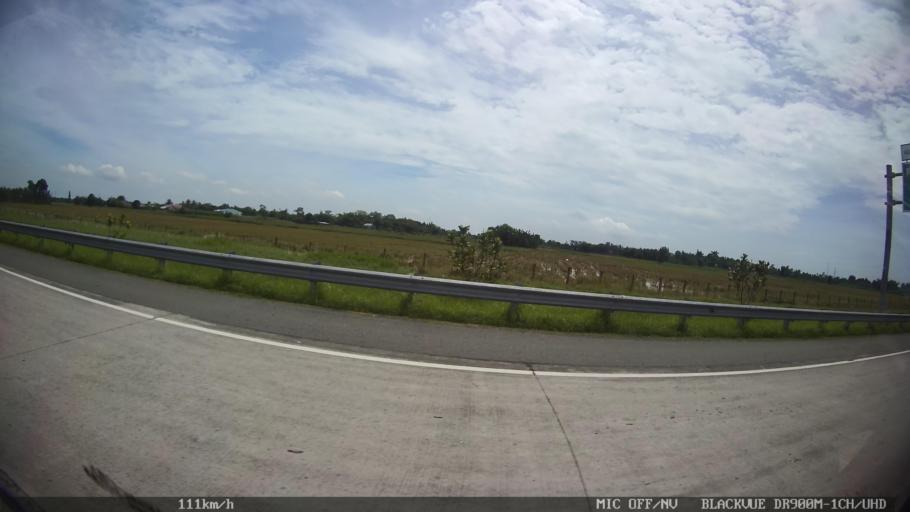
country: ID
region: North Sumatra
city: Percut
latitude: 3.5685
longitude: 98.8484
